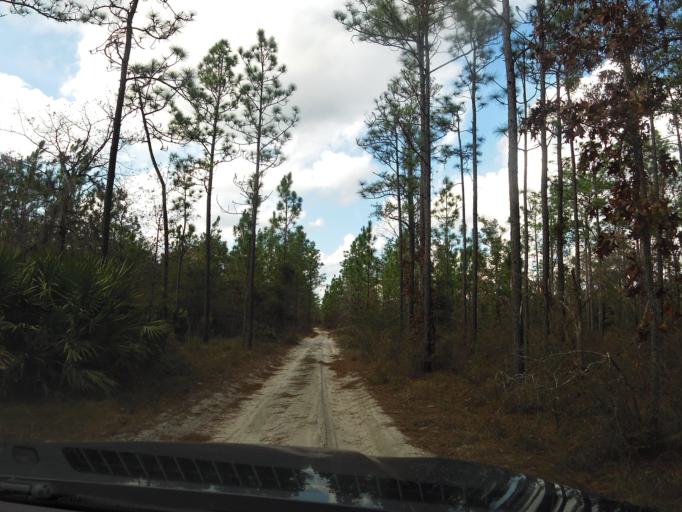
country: US
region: Florida
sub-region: Clay County
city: Middleburg
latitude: 30.1482
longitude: -81.9594
